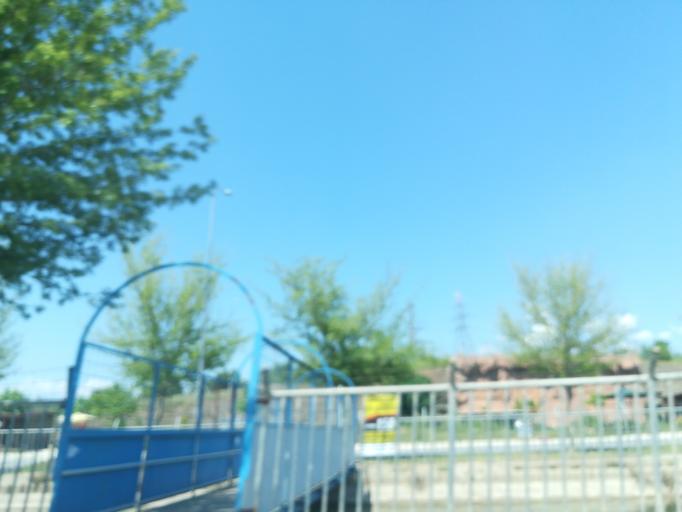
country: TR
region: Adana
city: Adana
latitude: 37.0305
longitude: 35.3511
